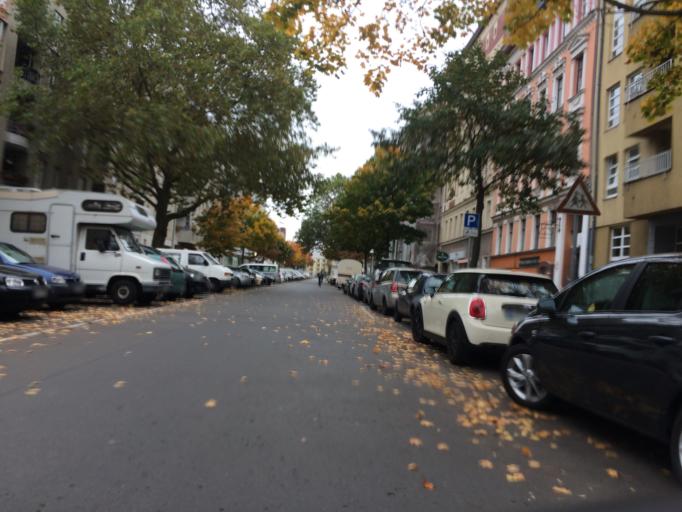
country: DE
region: Berlin
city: Gesundbrunnen
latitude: 52.5536
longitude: 13.3867
